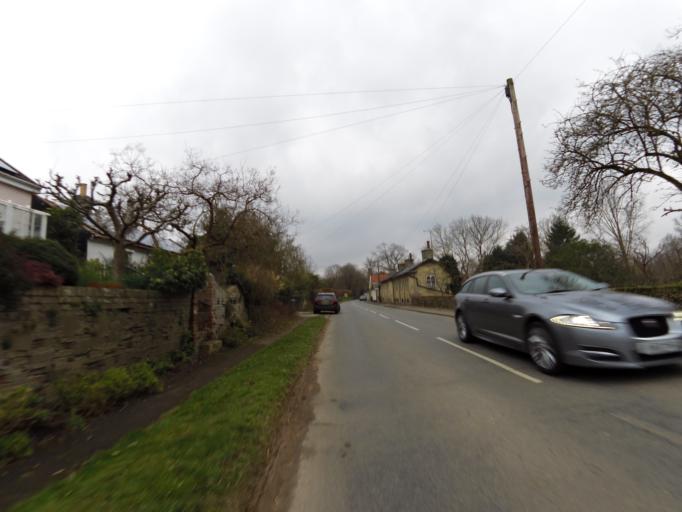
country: GB
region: England
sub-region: Suffolk
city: Wickham Market
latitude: 52.1788
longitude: 1.3389
